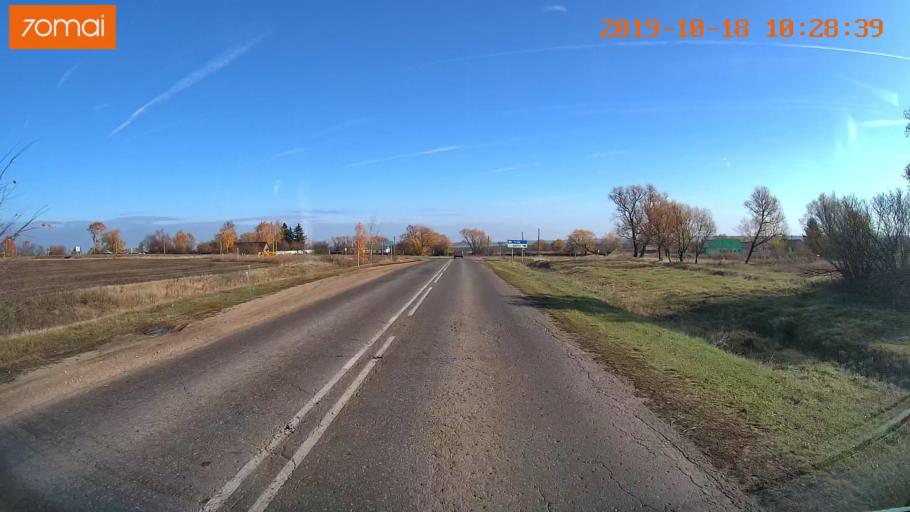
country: RU
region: Tula
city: Kurkino
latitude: 53.4461
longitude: 38.6585
